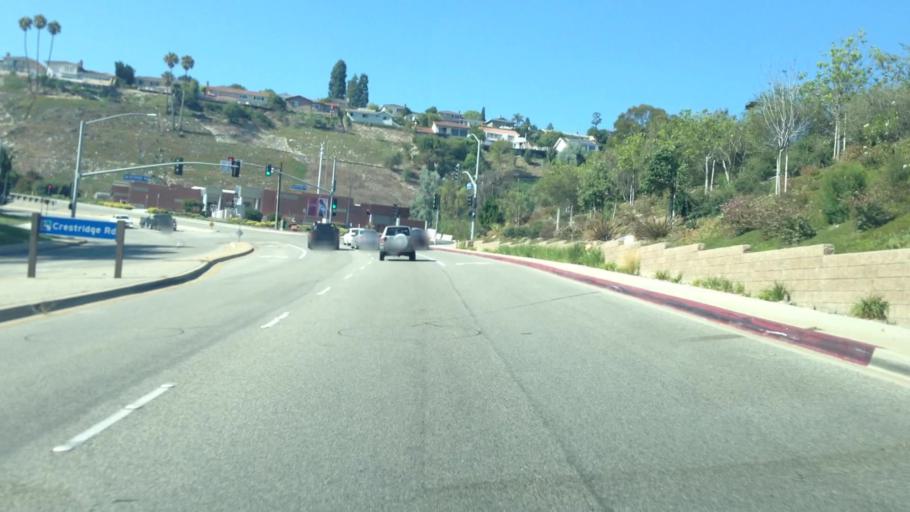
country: US
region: California
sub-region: Los Angeles County
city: Rolling Hills
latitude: 33.7678
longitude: -118.3714
